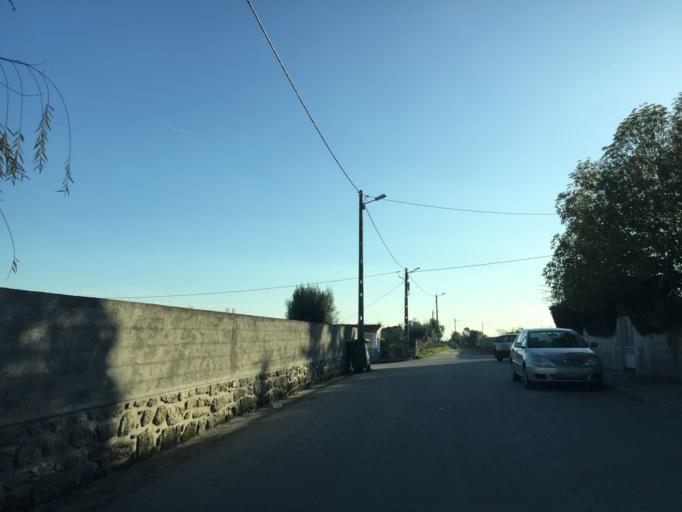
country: PT
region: Viseu
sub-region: Concelho de Carregal do Sal
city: Carregal do Sal
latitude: 40.4705
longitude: -7.9187
